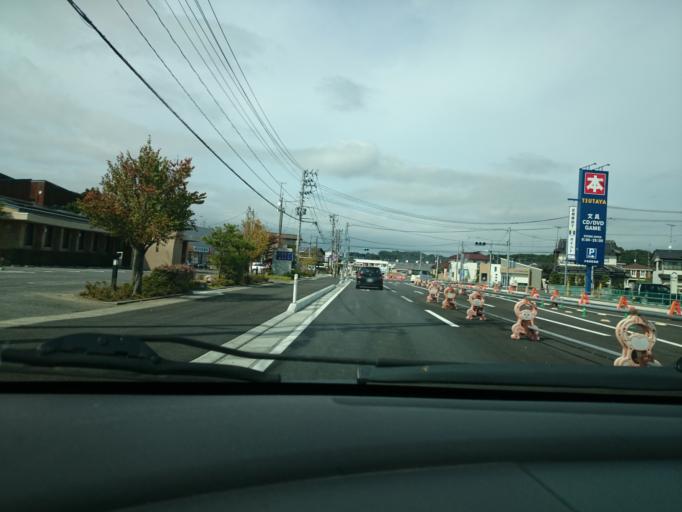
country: JP
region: Fukushima
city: Iwaki
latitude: 36.9774
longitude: 140.8884
